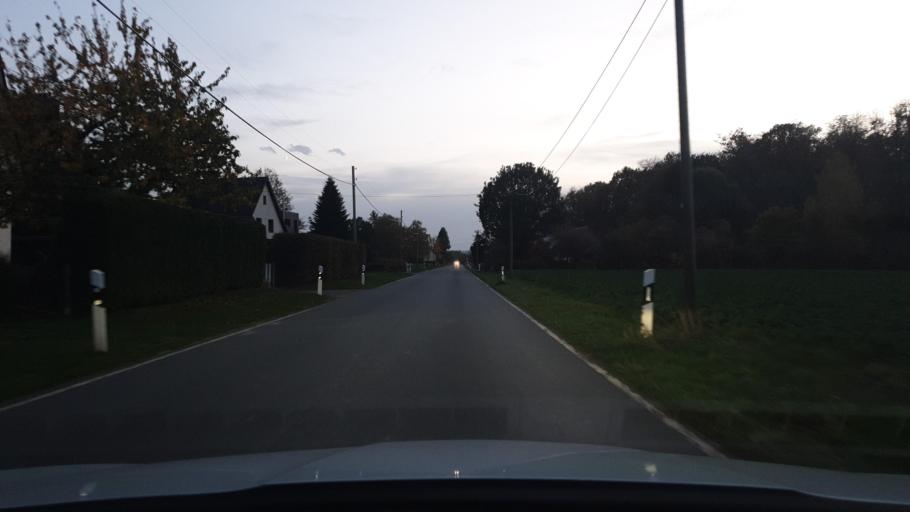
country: DE
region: North Rhine-Westphalia
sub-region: Regierungsbezirk Detmold
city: Bielefeld
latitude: 52.0649
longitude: 8.5770
